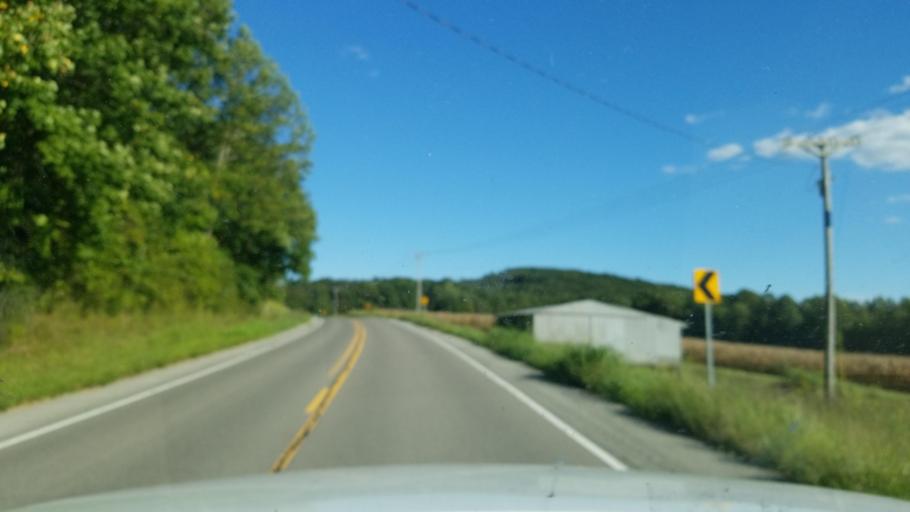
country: US
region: Illinois
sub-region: Hardin County
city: Rosiclare
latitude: 37.5765
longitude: -88.4307
